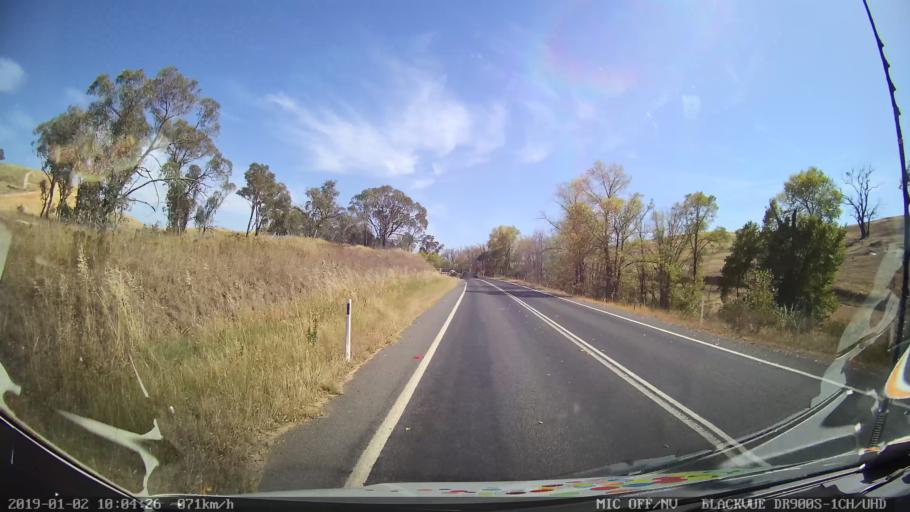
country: AU
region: New South Wales
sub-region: Gundagai
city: Gundagai
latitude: -35.1677
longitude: 148.1232
